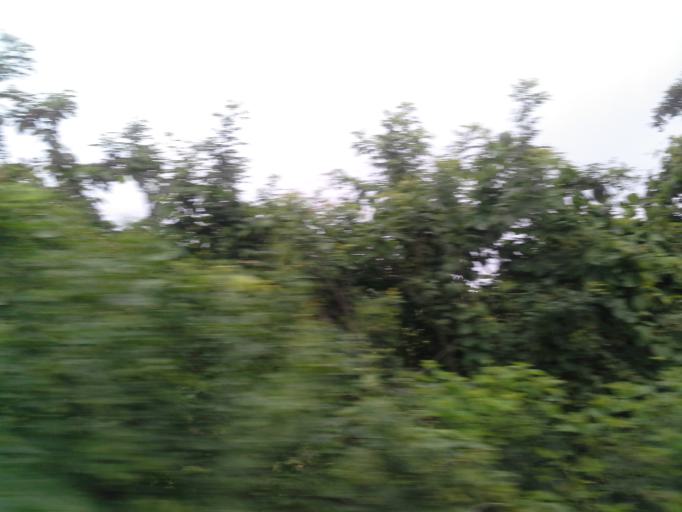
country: CO
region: Sucre
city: Ovejas
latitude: 9.5005
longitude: -75.1536
